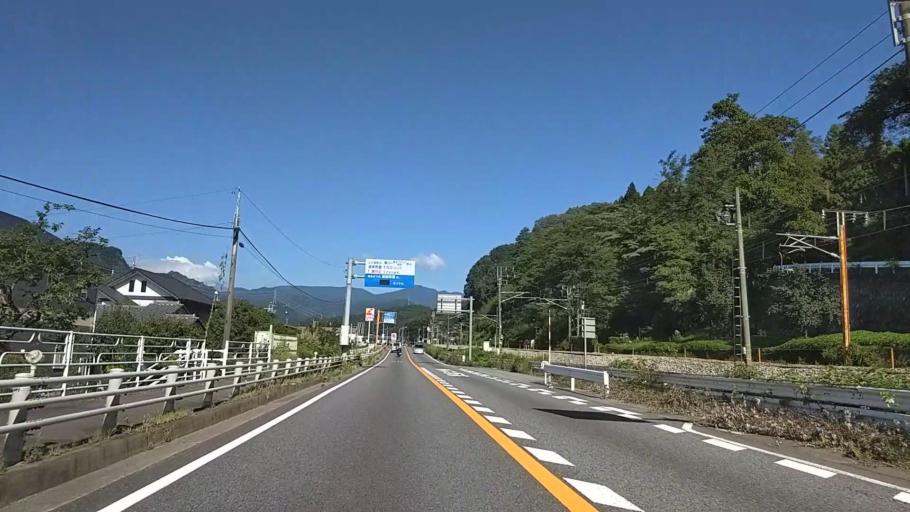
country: JP
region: Gunma
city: Annaka
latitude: 36.3278
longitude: 138.7561
